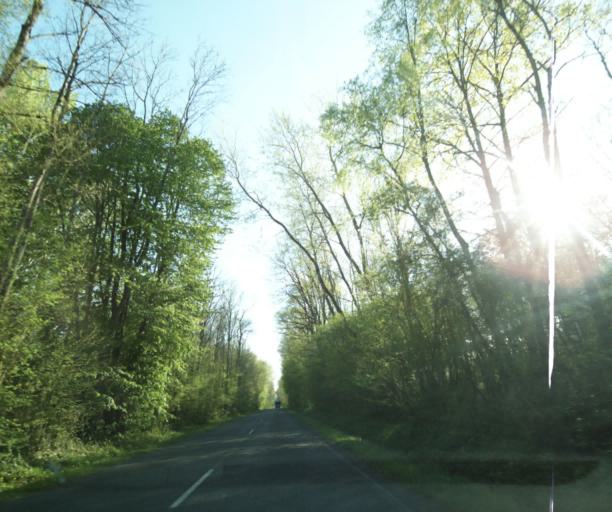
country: FR
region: Ile-de-France
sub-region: Departement de Seine-et-Marne
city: Nangis
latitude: 48.5360
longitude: 2.9857
